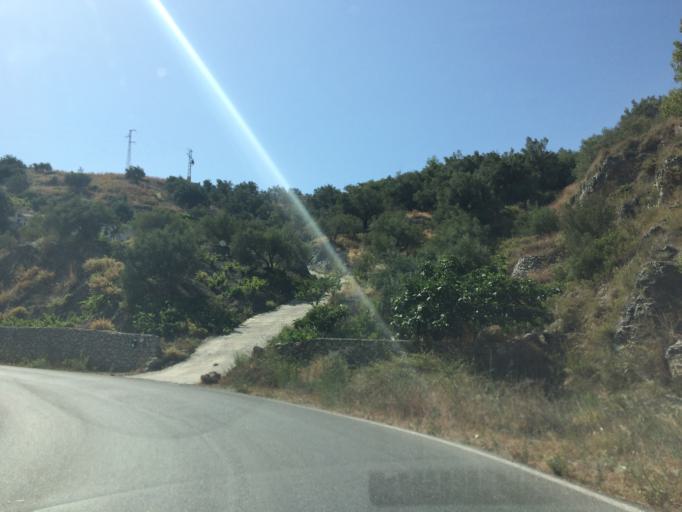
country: ES
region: Andalusia
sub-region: Provincia de Malaga
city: Frigiliana
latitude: 36.8020
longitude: -3.9088
